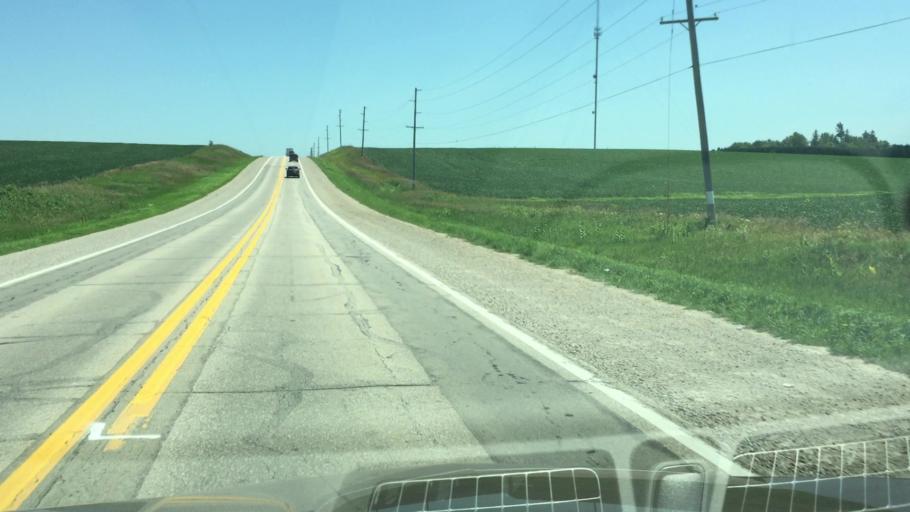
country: US
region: Iowa
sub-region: Cedar County
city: Mechanicsville
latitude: 41.8885
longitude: -91.1796
